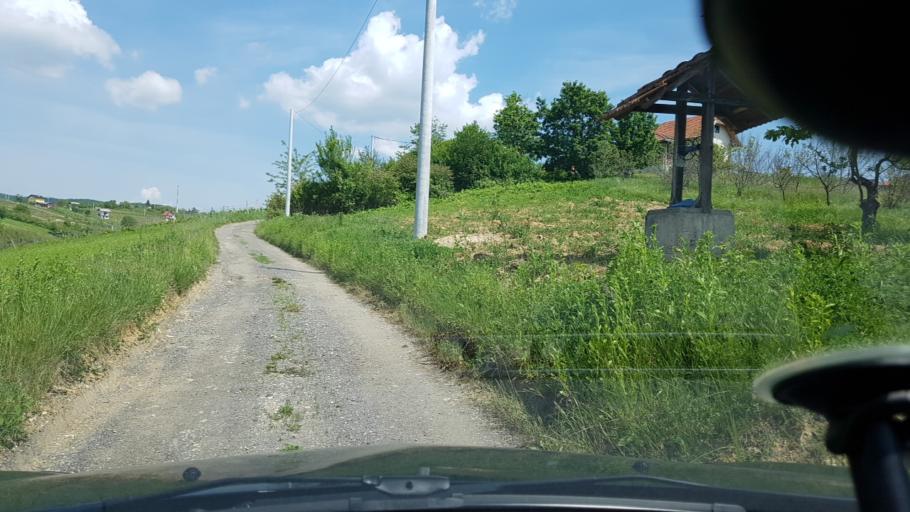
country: HR
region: Krapinsko-Zagorska
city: Marija Bistrica
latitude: 45.9371
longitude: 16.2099
